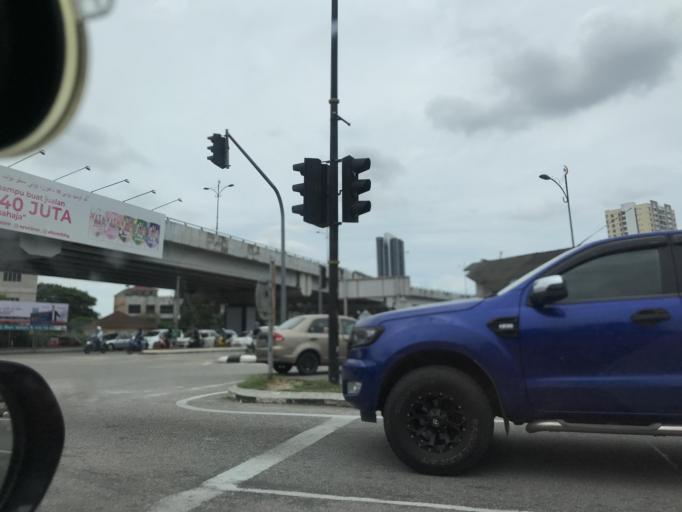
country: MY
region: Kelantan
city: Kota Bharu
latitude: 6.1157
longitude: 102.2364
